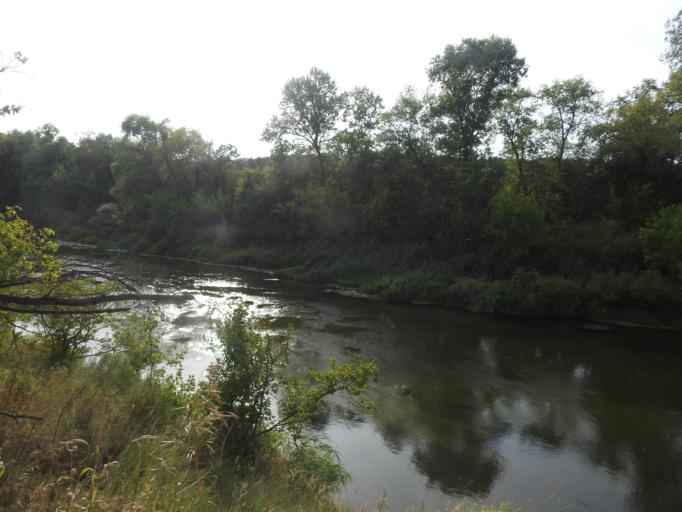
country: RU
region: Saratov
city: Lysyye Gory
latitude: 51.2898
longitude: 45.0025
